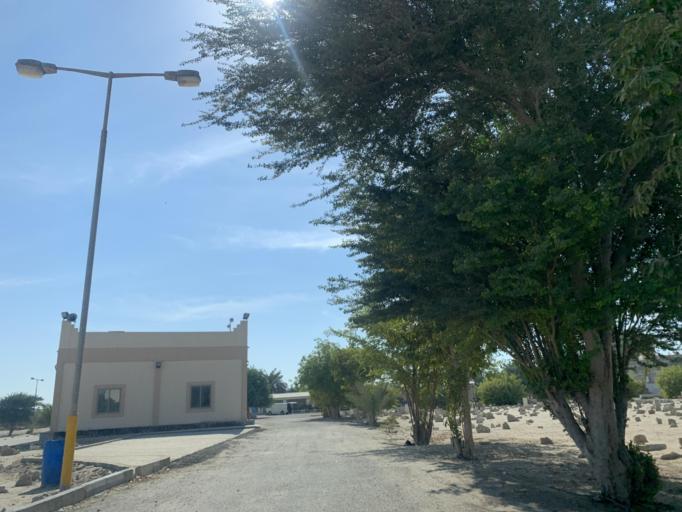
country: BH
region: Central Governorate
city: Madinat Hamad
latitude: 26.1147
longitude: 50.4835
